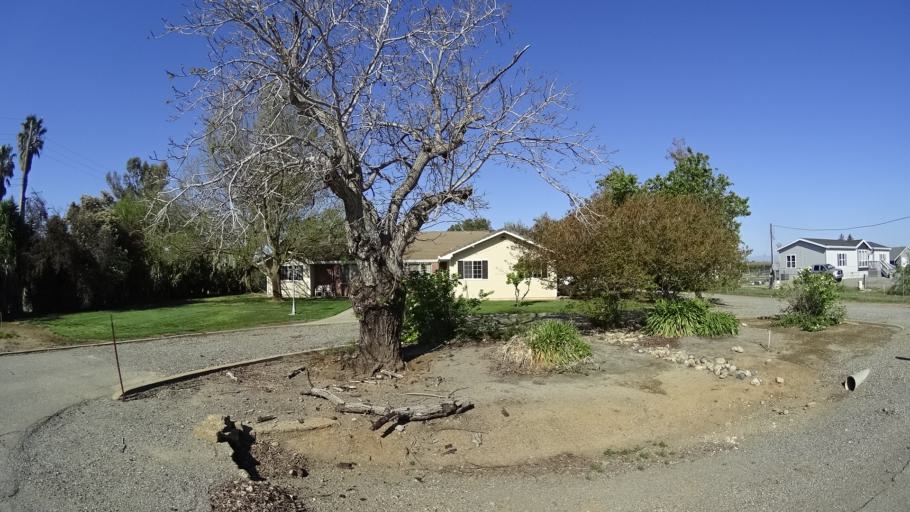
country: US
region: California
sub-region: Glenn County
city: Willows
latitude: 39.5445
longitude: -122.1982
